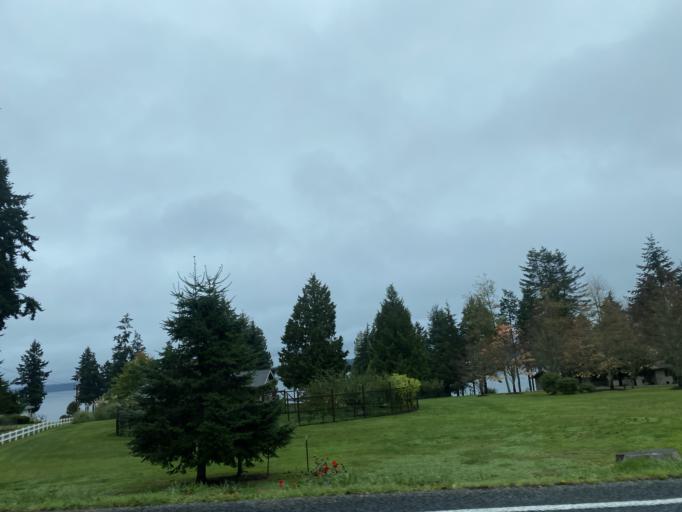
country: US
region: Washington
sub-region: Island County
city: Langley
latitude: 48.0484
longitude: -122.4412
